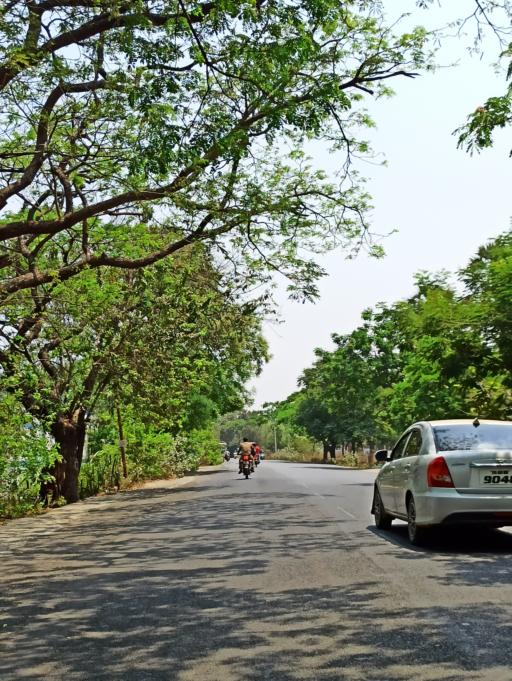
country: IN
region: Tamil Nadu
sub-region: Thiruvallur
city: Chinnasekkadu
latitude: 13.1544
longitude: 80.2437
